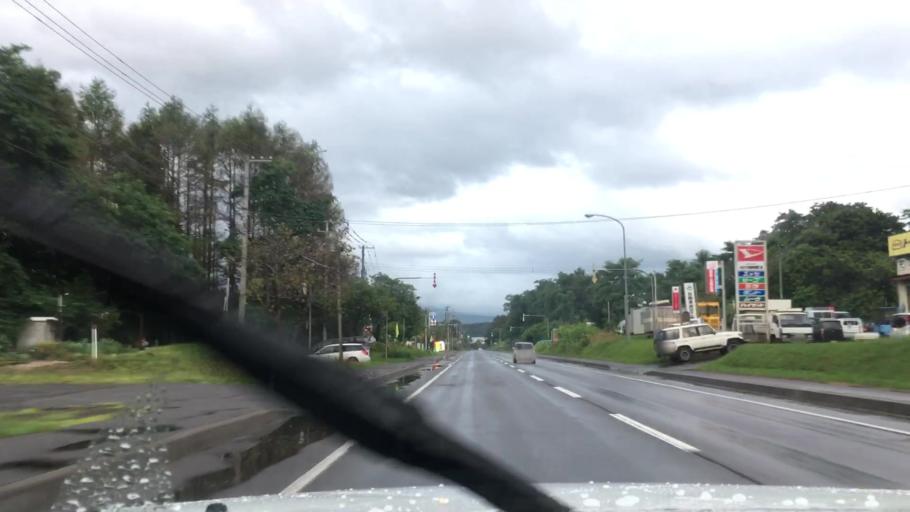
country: JP
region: Hokkaido
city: Nanae
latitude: 42.1092
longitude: 140.5528
